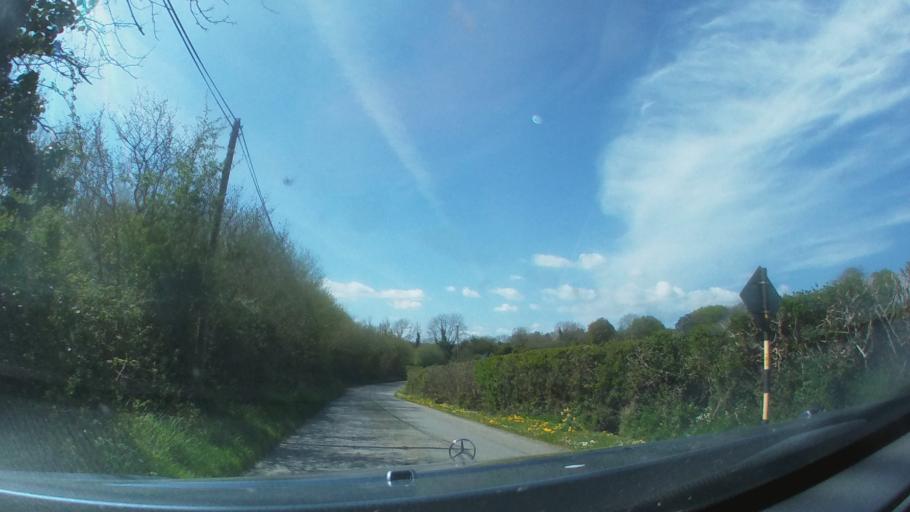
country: IE
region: Leinster
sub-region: Kilkenny
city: Callan
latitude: 52.6261
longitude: -7.4549
